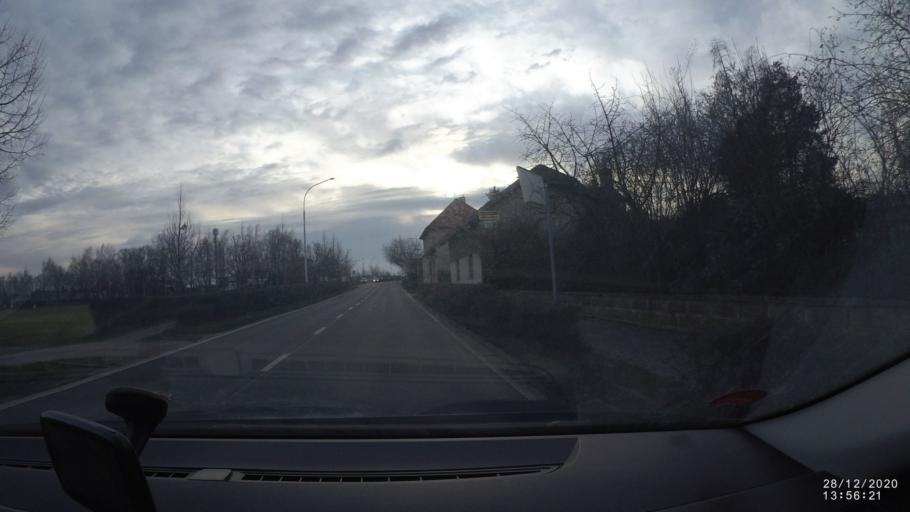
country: CZ
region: Central Bohemia
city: Sestajovice
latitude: 50.1071
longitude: 14.6808
